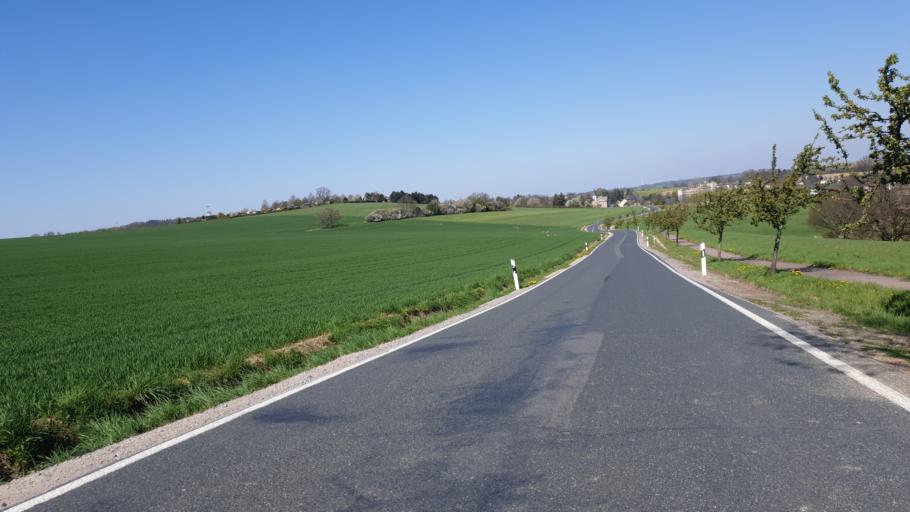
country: DE
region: Saxony
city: Taura
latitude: 50.9131
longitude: 12.8543
